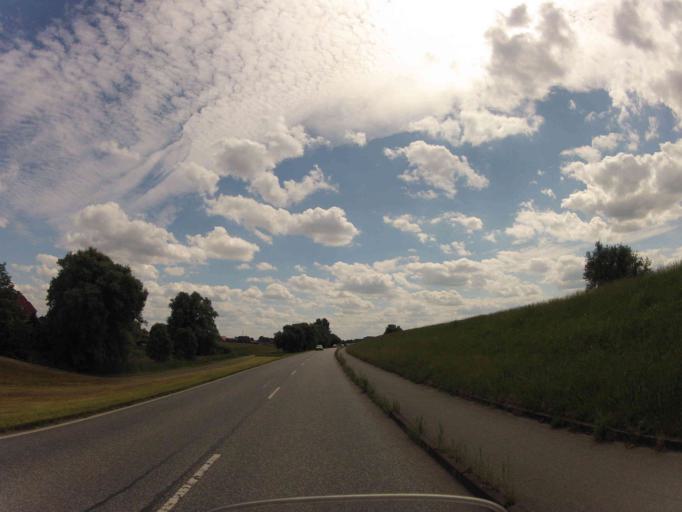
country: DE
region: Hamburg
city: Rothenburgsort
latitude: 53.4728
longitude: 10.0651
